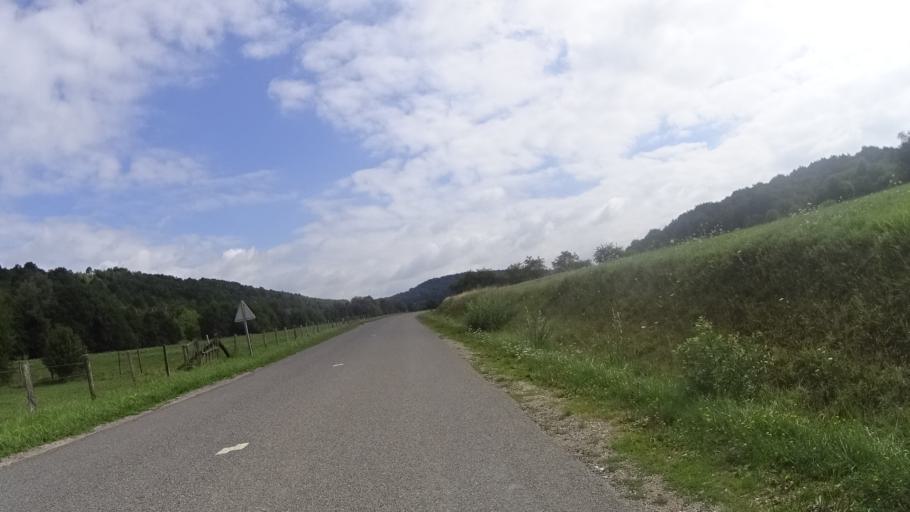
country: FR
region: Lorraine
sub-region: Departement de la Meuse
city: Velaines
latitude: 48.7140
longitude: 5.3076
